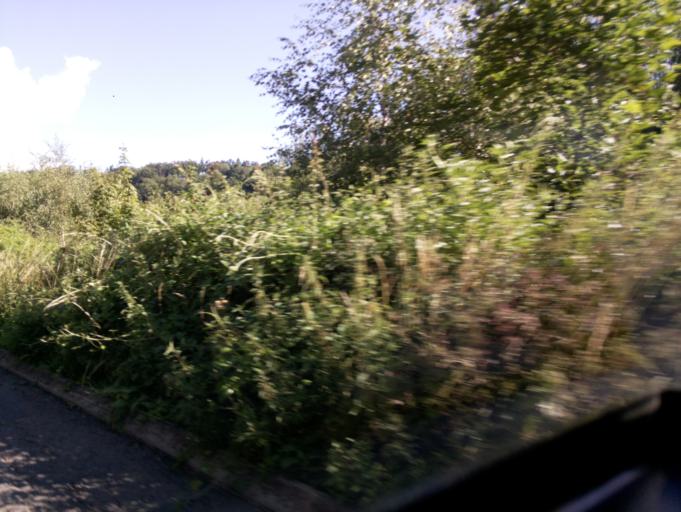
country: GB
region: England
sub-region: Gloucestershire
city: Lydbrook
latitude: 51.8527
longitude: -2.5912
